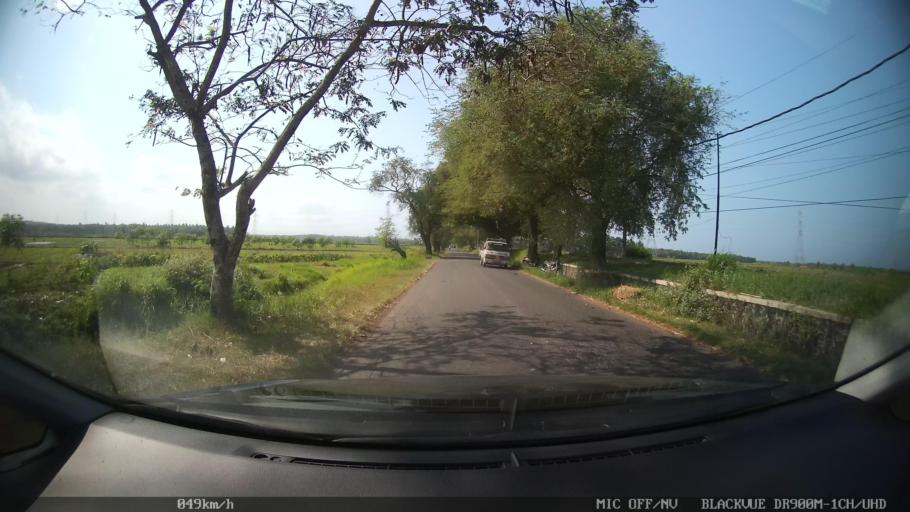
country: ID
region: Daerah Istimewa Yogyakarta
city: Srandakan
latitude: -7.9152
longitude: 110.1790
